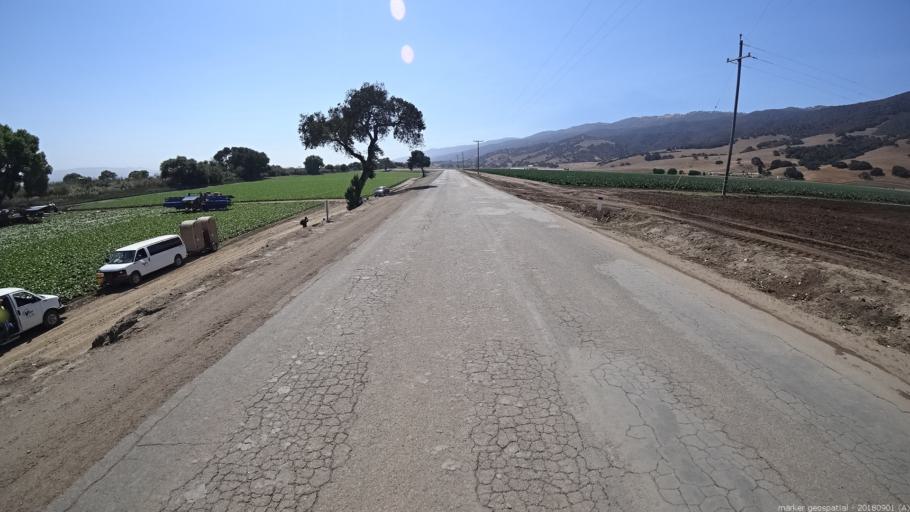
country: US
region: California
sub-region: Monterey County
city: Chualar
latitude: 36.5450
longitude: -121.5451
